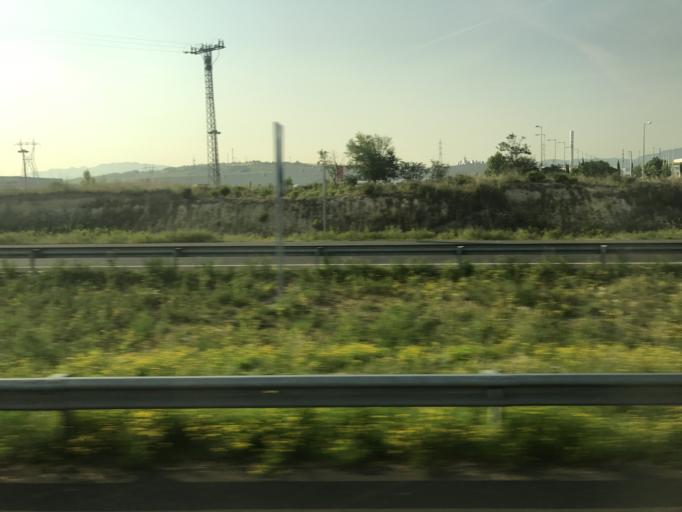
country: ES
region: Castille and Leon
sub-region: Provincia de Burgos
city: Miranda de Ebro
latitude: 42.7024
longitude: -2.9197
